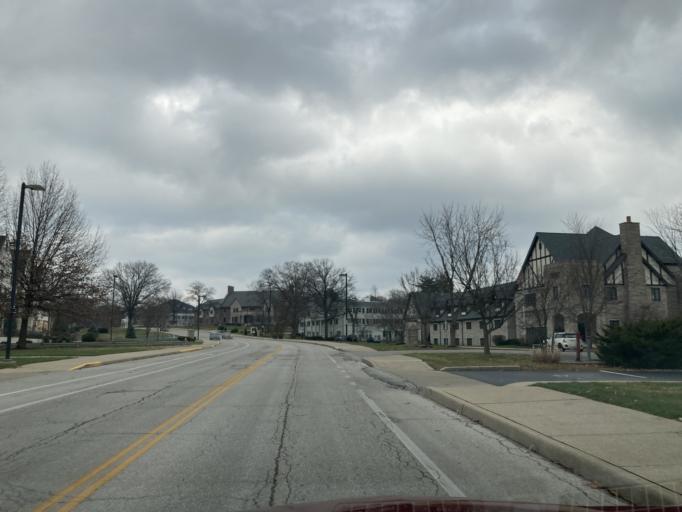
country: US
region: Indiana
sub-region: Monroe County
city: Bloomington
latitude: 39.1757
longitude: -86.5136
